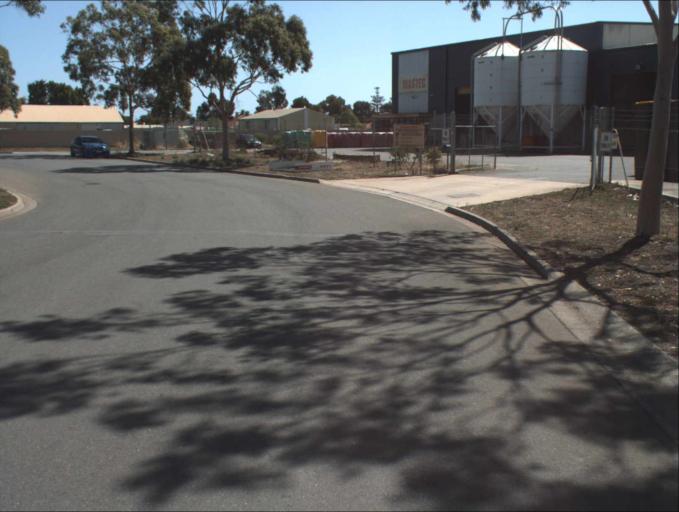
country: AU
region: South Australia
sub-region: Port Adelaide Enfield
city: Alberton
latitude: -34.8462
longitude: 138.5423
